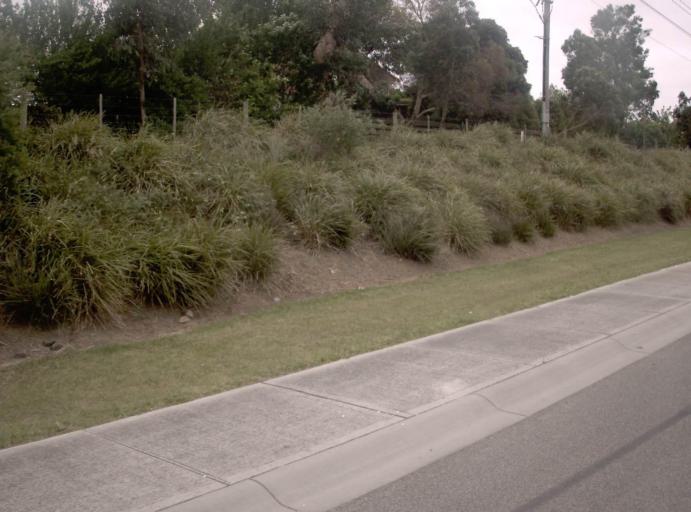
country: AU
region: Victoria
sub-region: Casey
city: Endeavour Hills
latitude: -37.9844
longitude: 145.2774
